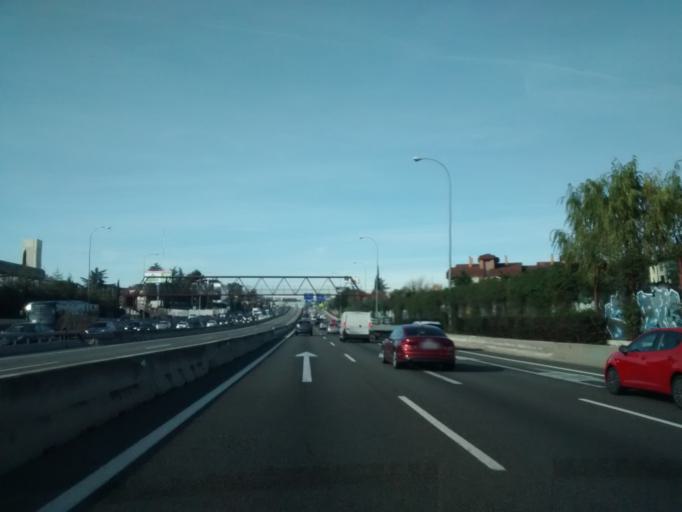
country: ES
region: Madrid
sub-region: Provincia de Madrid
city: Majadahonda
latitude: 40.4812
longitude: -3.8522
